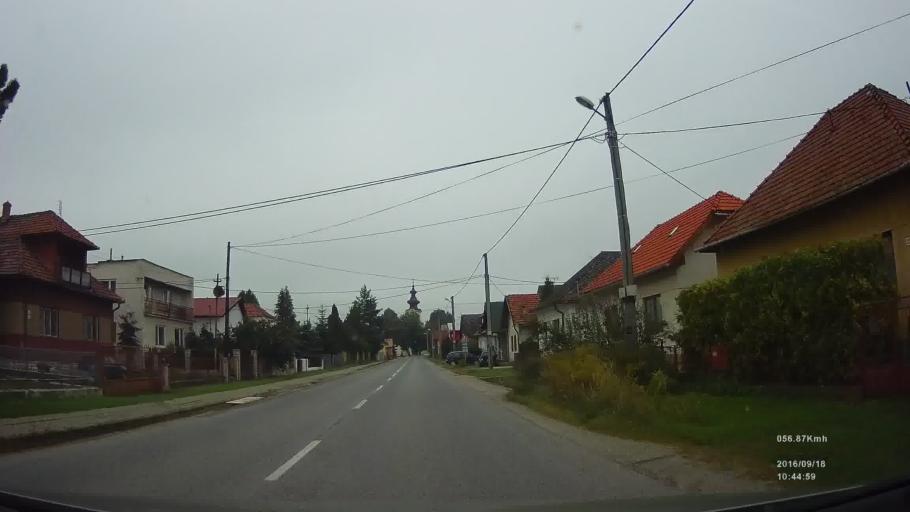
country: SK
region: Kosicky
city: Spisska Nova Ves
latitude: 48.9594
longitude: 20.5825
